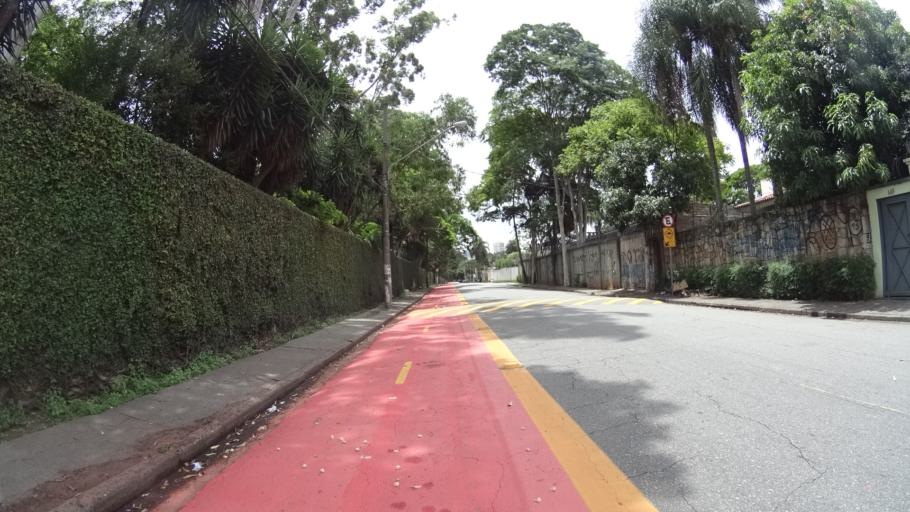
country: BR
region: Sao Paulo
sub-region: Sao Paulo
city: Sao Paulo
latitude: -23.5847
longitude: -46.6974
